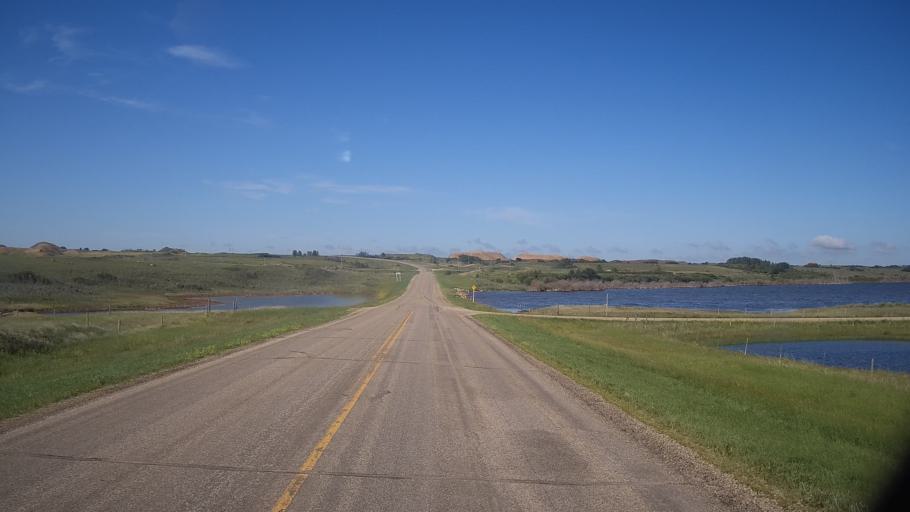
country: CA
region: Saskatchewan
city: Watrous
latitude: 51.7120
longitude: -105.3719
